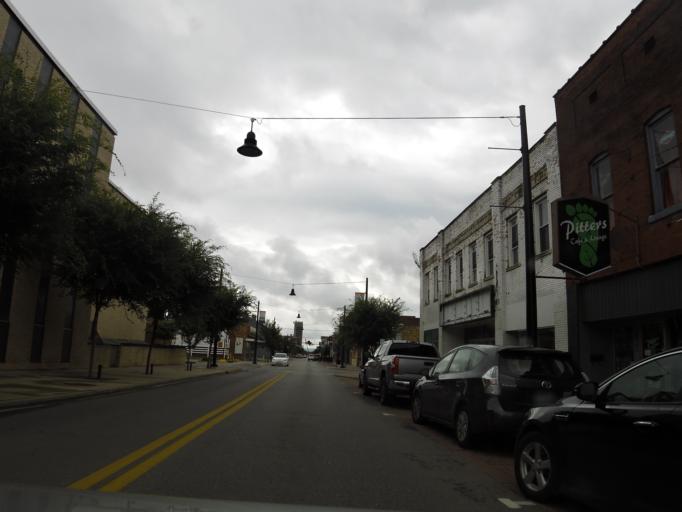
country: US
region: Missouri
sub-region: Cape Girardeau County
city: Cape Girardeau
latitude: 37.3069
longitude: -89.5288
